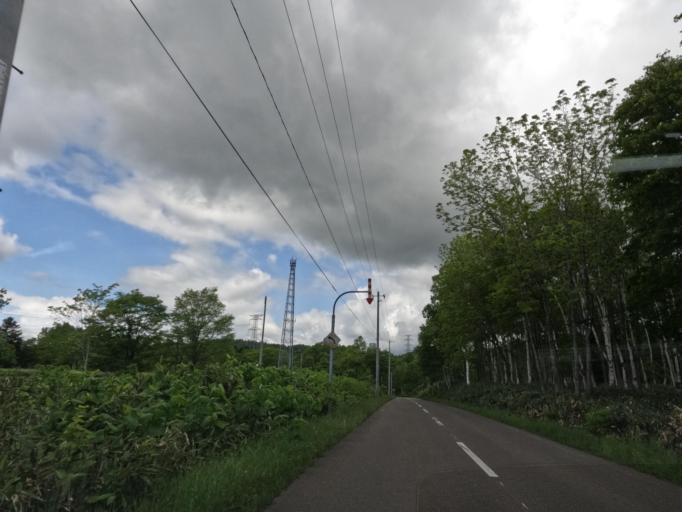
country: JP
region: Hokkaido
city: Tobetsu
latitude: 43.4631
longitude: 141.5986
